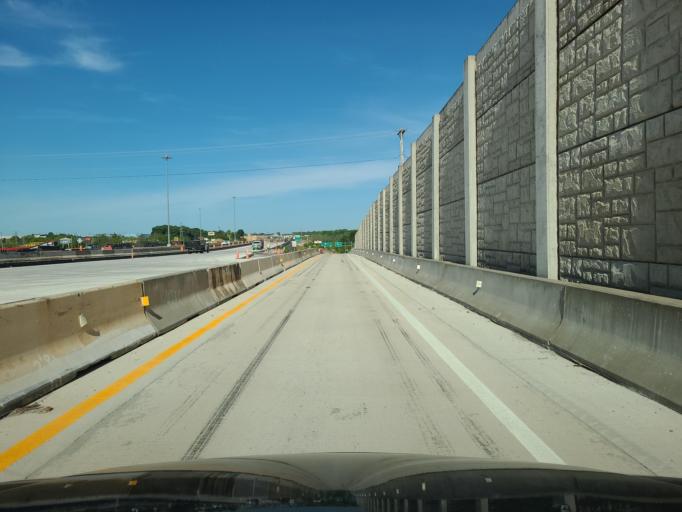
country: US
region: North Carolina
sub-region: Iredell County
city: Statesville
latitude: 35.8064
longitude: -80.8795
